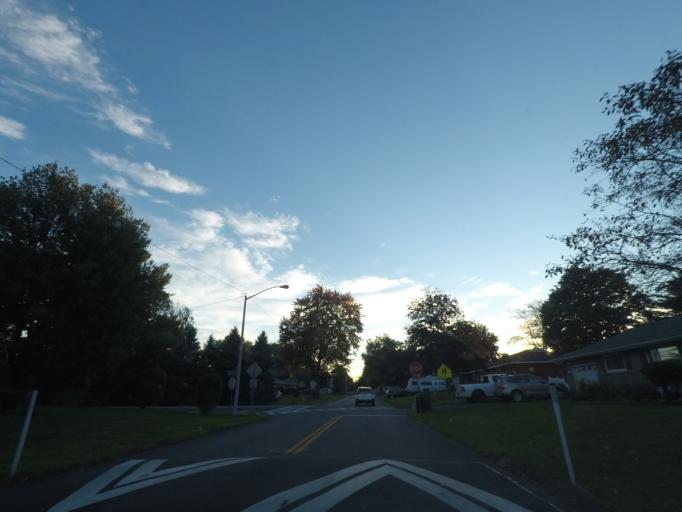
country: US
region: New York
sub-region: Albany County
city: Colonie
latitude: 42.7221
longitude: -73.8233
